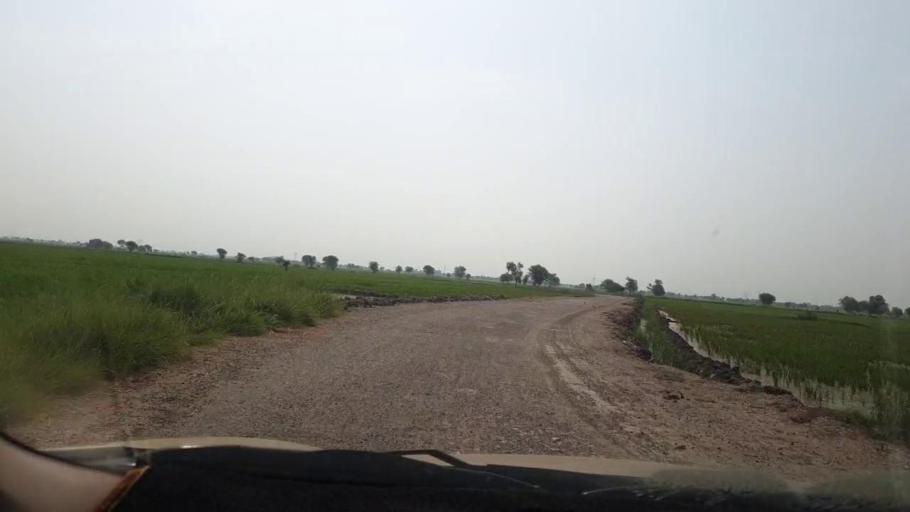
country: PK
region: Sindh
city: Goth Garelo
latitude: 27.4461
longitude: 68.0356
